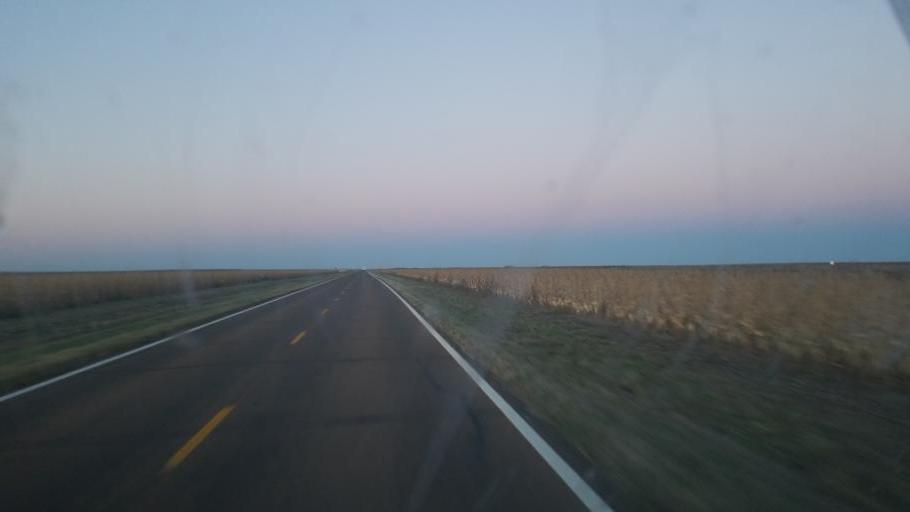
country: US
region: Kansas
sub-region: Wallace County
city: Sharon Springs
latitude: 38.9418
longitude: -101.5133
